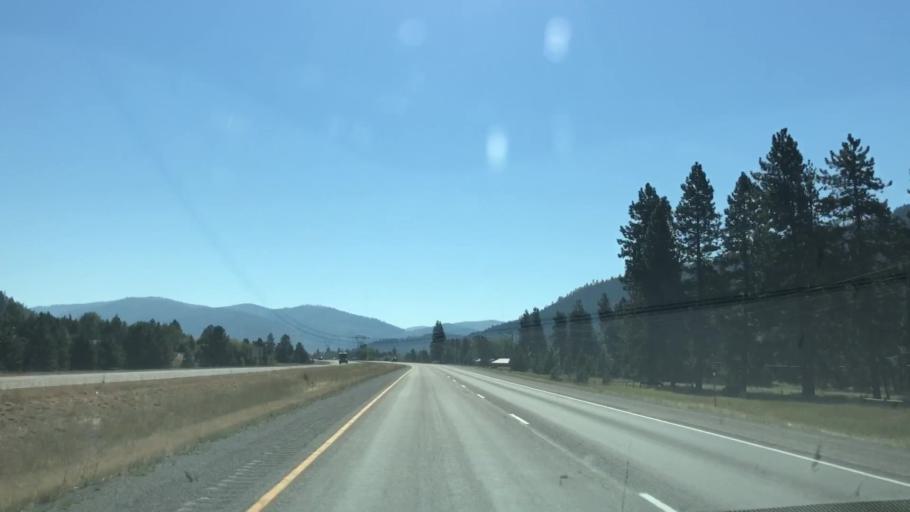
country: US
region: Montana
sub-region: Missoula County
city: Clinton
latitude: 46.8039
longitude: -113.7722
